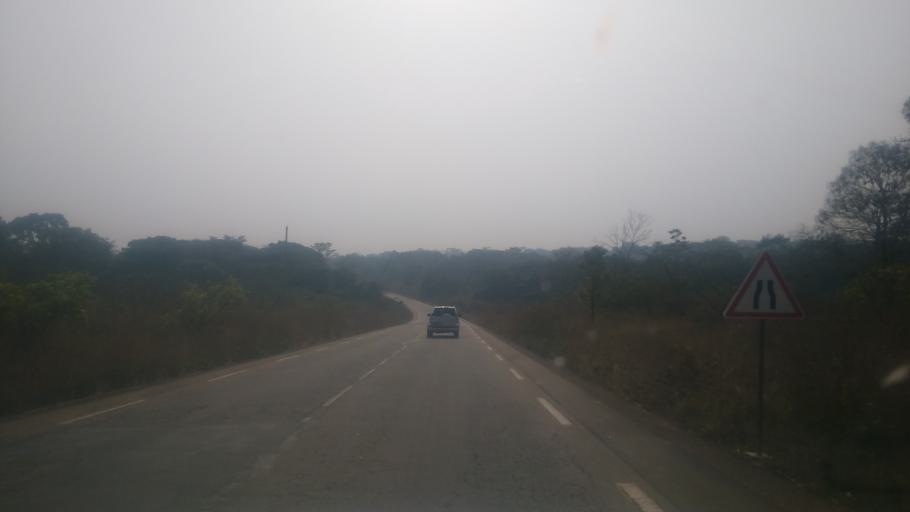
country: CM
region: Centre
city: Ndikinimeki
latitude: 4.8013
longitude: 10.9738
